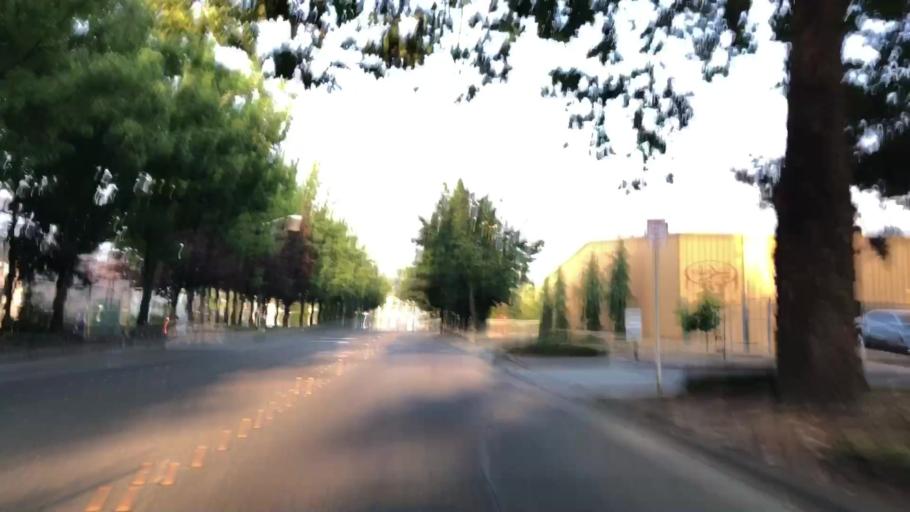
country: US
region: Washington
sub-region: King County
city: Redmond
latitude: 47.6721
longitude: -122.0973
